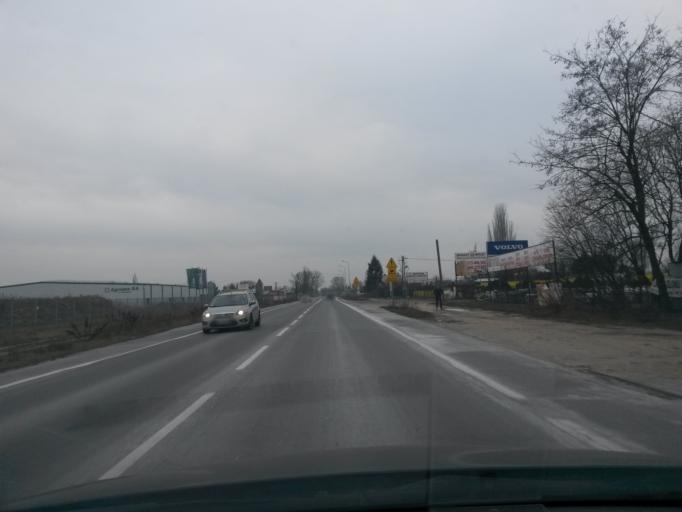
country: PL
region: Greater Poland Voivodeship
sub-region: Powiat poznanski
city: Kobylnica
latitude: 52.4388
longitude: 17.0400
